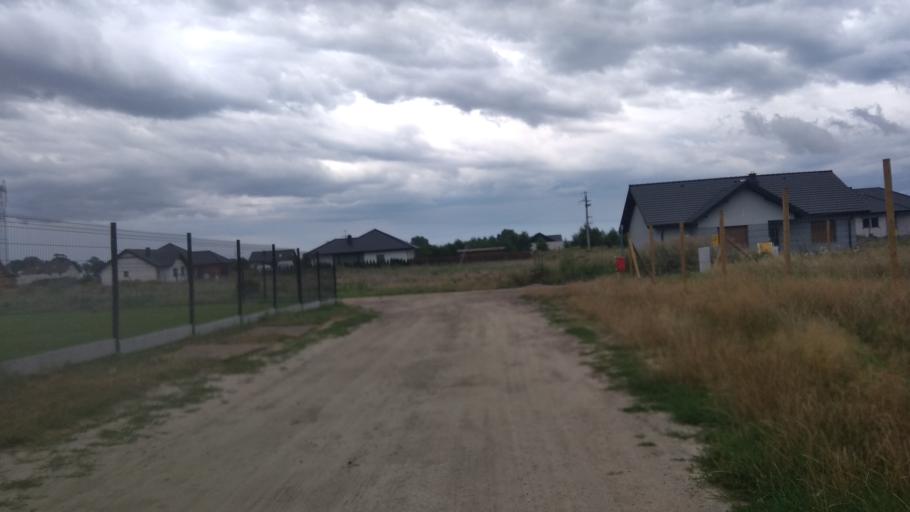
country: PL
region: Kujawsko-Pomorskie
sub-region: Powiat bydgoski
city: Osielsko
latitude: 53.2166
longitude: 18.1359
